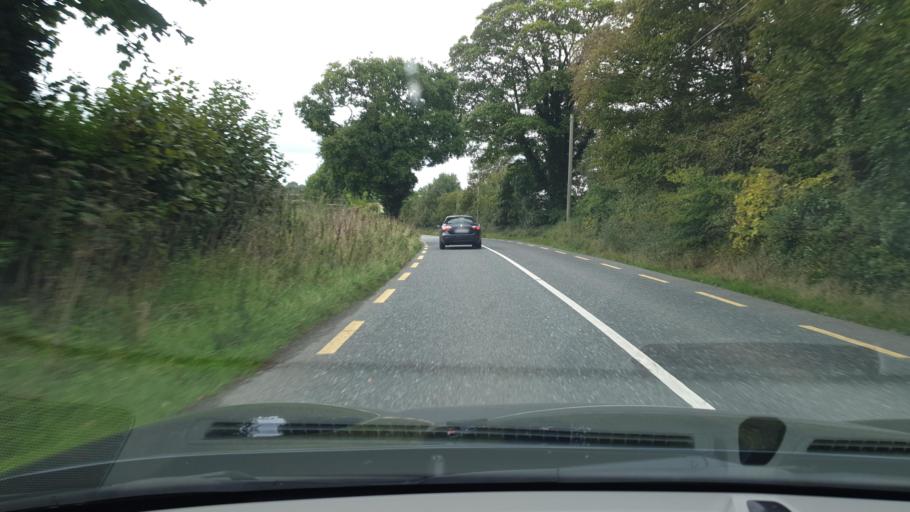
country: IE
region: Leinster
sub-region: Kildare
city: Clane
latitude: 53.2756
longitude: -6.6909
